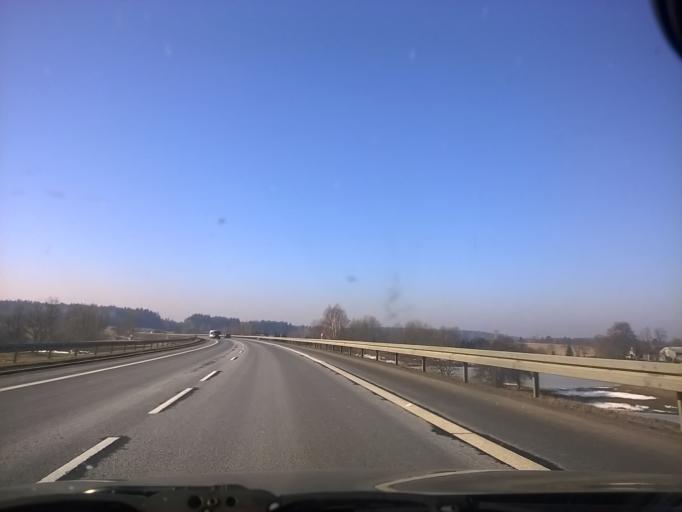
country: PL
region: Warmian-Masurian Voivodeship
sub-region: Powiat olsztynski
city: Barczewo
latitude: 53.8283
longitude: 20.7950
